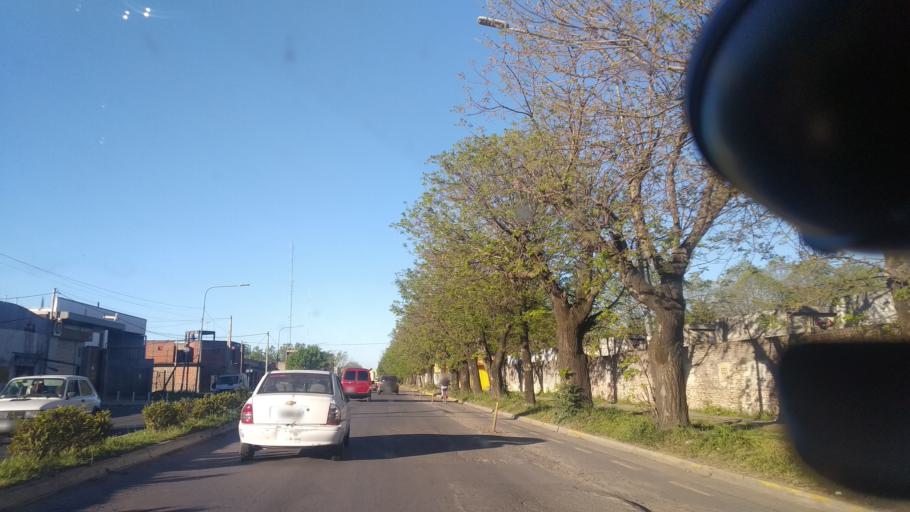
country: AR
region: Buenos Aires
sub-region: Partido de La Plata
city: La Plata
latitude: -34.9592
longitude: -57.9587
